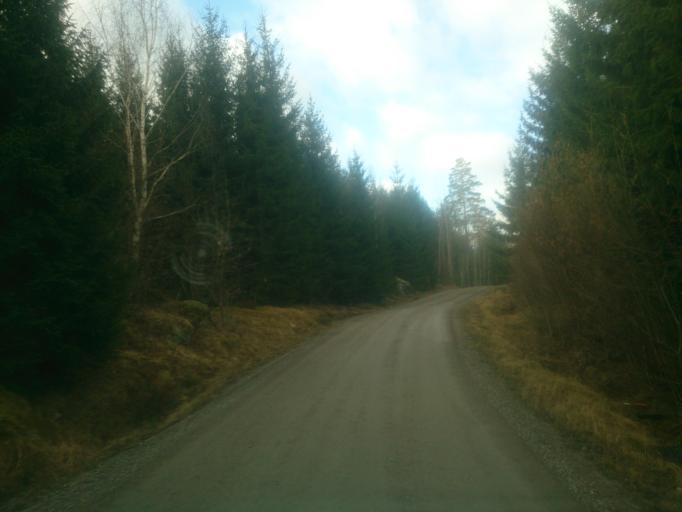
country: SE
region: OEstergoetland
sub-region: Atvidabergs Kommun
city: Atvidaberg
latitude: 58.1998
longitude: 16.1540
